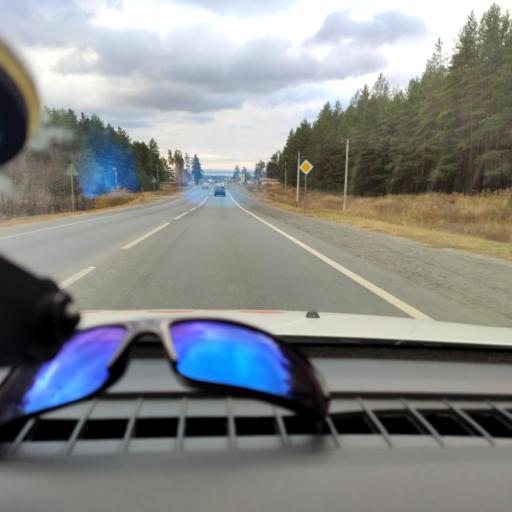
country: RU
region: Samara
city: Volzhskiy
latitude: 53.4420
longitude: 50.1236
